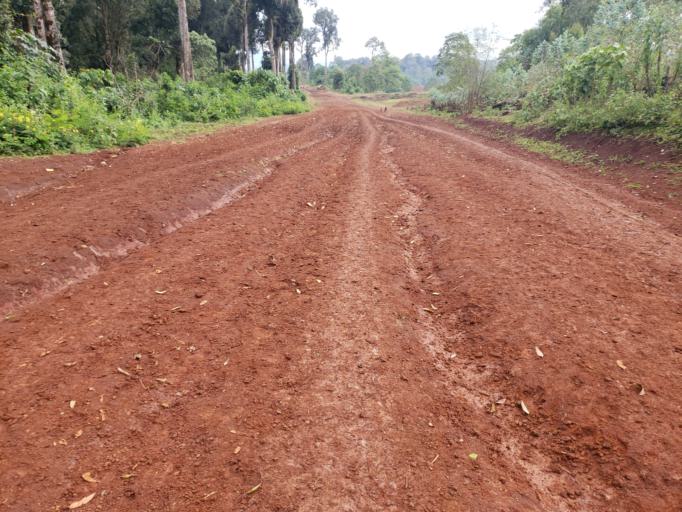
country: ET
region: Oromiya
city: Dodola
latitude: 6.5541
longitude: 39.4230
